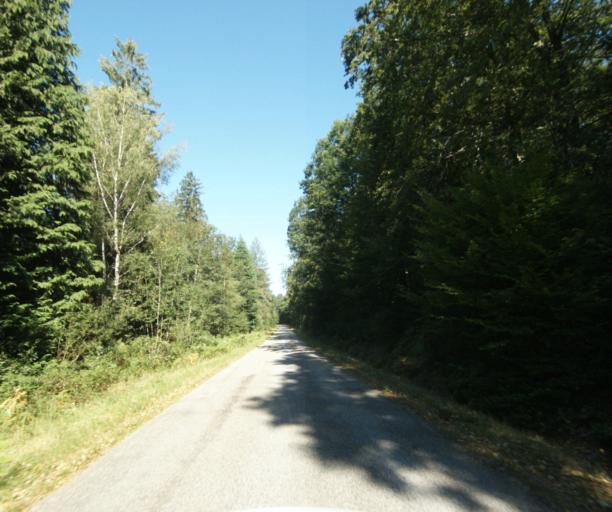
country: FR
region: Lorraine
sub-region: Departement des Vosges
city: Epinal
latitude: 48.1464
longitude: 6.4801
